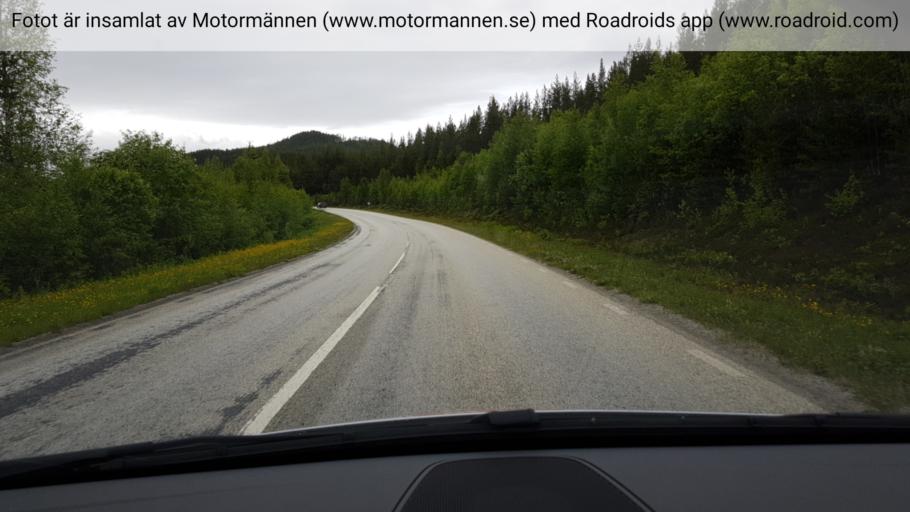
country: SE
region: Jaemtland
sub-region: Harjedalens Kommun
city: Sveg
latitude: 62.4140
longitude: 13.6325
